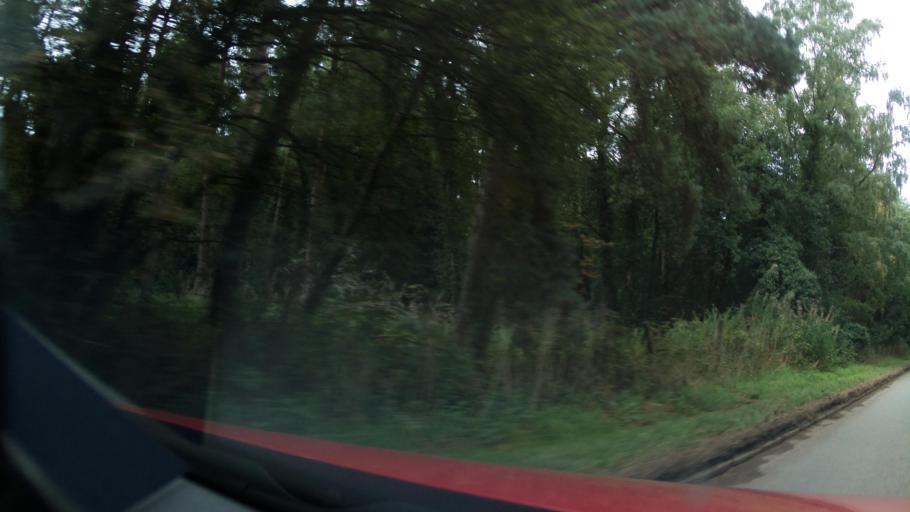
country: GB
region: England
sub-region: Staffordshire
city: Eccleshall
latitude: 52.8968
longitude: -2.2150
